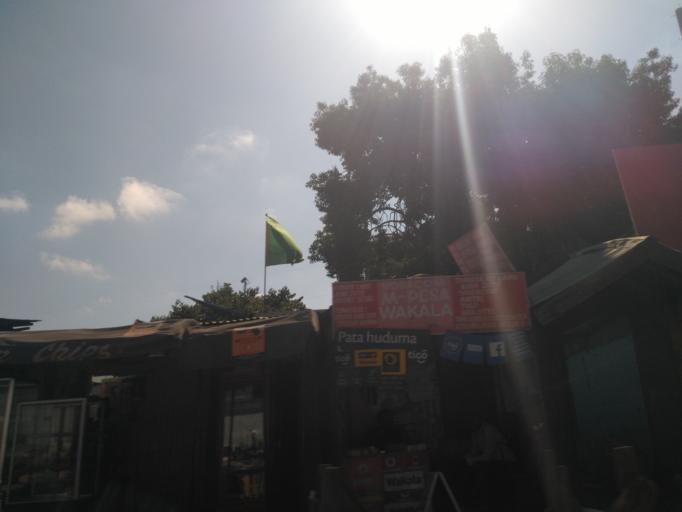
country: TZ
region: Arusha
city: Arusha
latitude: -3.3726
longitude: 36.6854
